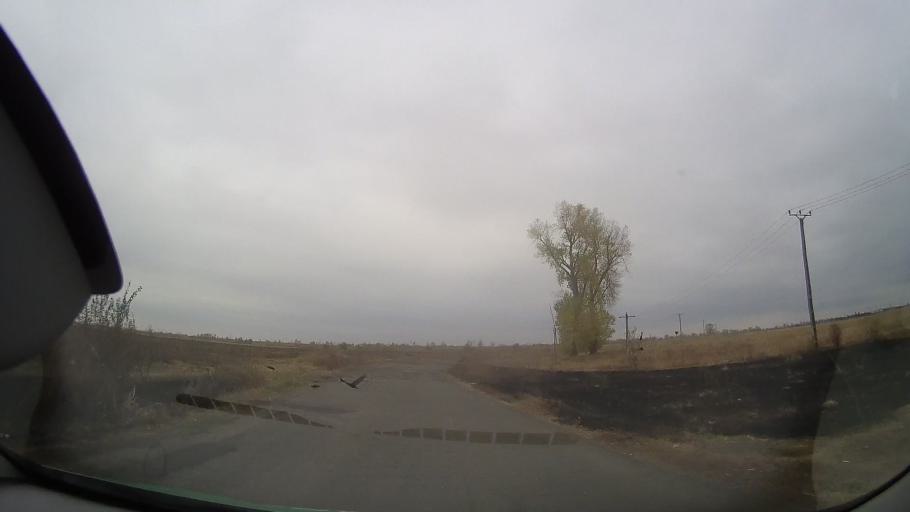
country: RO
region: Braila
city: Dudesti
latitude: 44.9344
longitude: 27.4266
